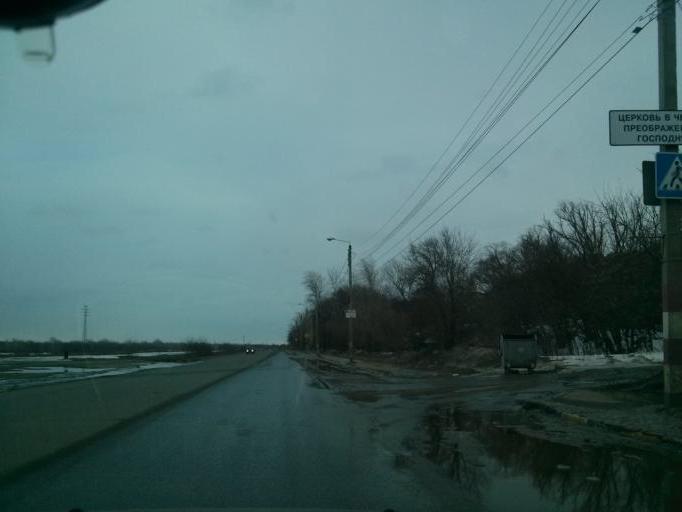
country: RU
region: Nizjnij Novgorod
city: Bor
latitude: 56.3211
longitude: 44.0673
